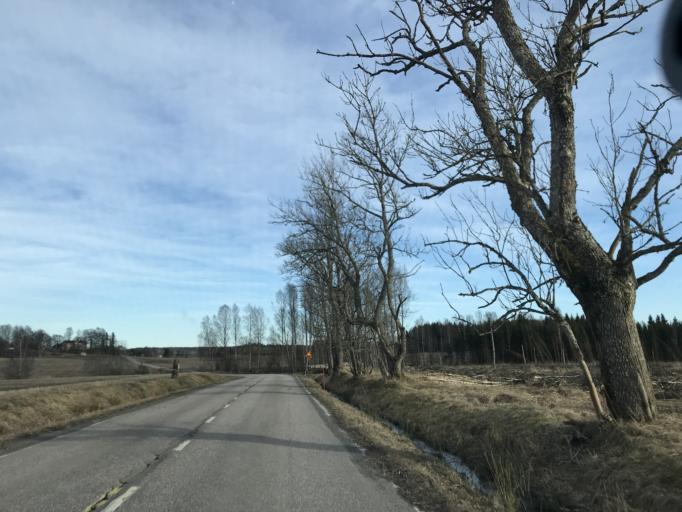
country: FI
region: Uusimaa
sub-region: Raaseporin
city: Pohja
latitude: 60.0906
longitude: 23.4943
